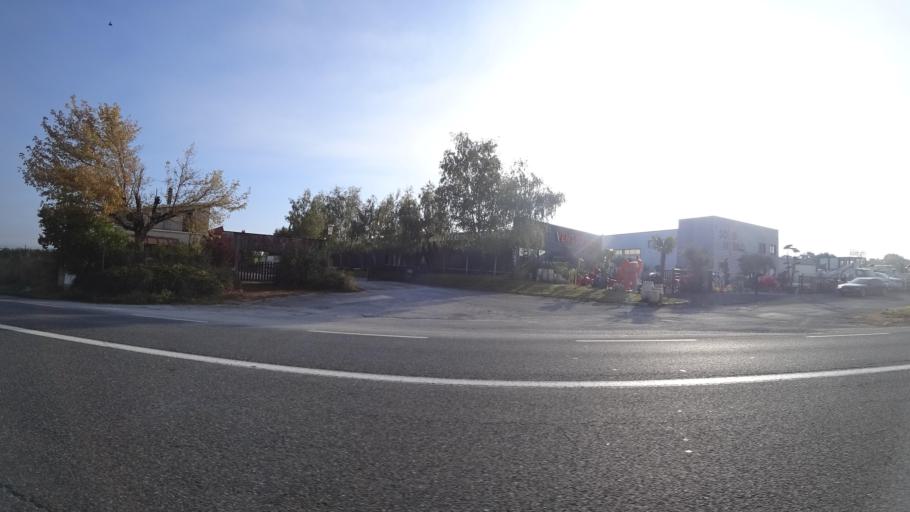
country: FR
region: Midi-Pyrenees
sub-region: Departement de l'Aveyron
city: Luc-la-Primaube
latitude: 44.3188
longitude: 2.5582
